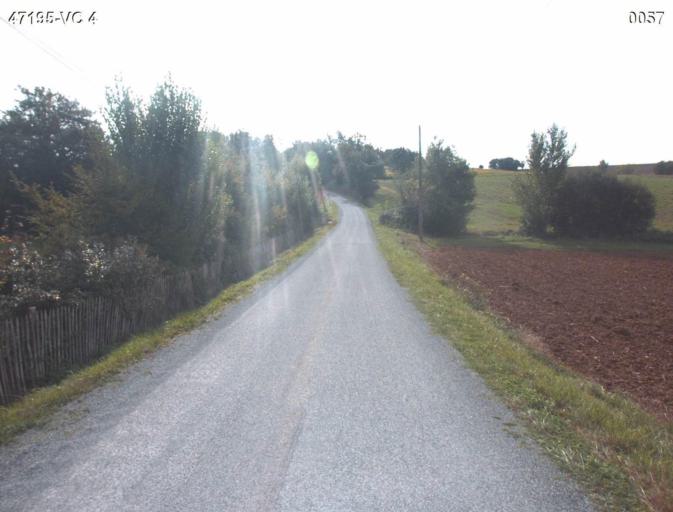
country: FR
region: Aquitaine
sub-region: Departement du Lot-et-Garonne
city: Nerac
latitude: 44.1201
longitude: 0.3756
